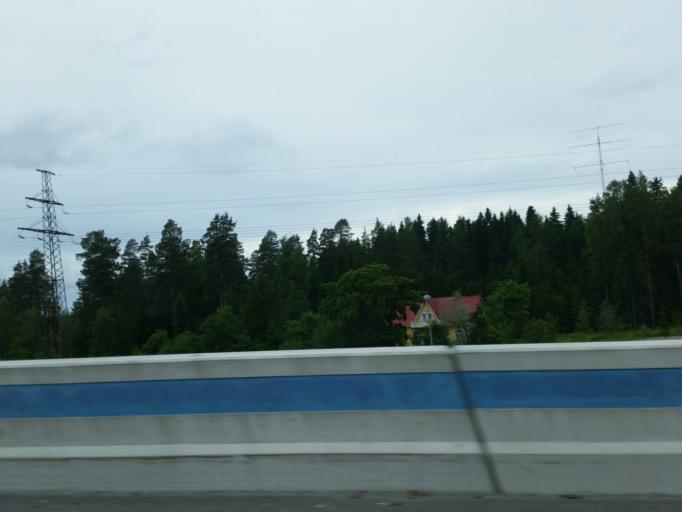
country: FI
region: Northern Savo
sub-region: Kuopio
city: Kuopio
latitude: 62.9503
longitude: 27.6752
